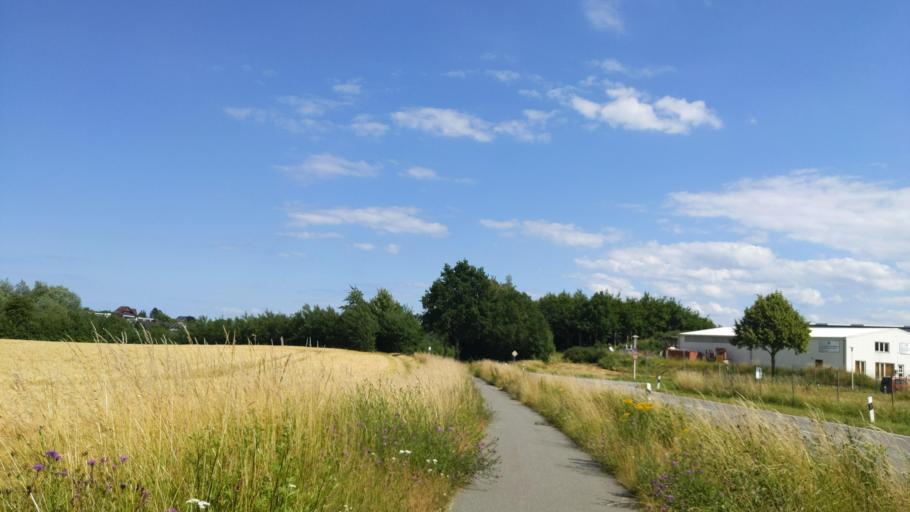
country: DE
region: Schleswig-Holstein
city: Gromitz
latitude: 54.1538
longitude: 10.9410
